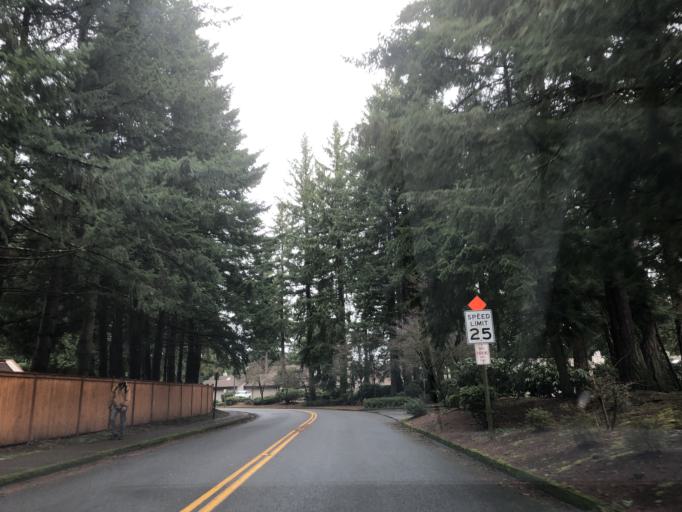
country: US
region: Washington
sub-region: King County
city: Fairwood
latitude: 47.4452
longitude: -122.1436
